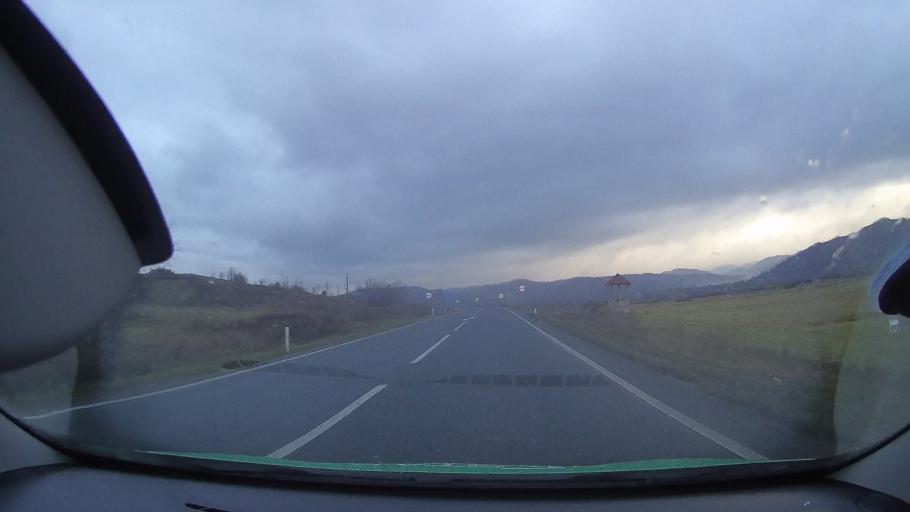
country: RO
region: Hunedoara
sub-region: Comuna Ribita
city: Ribita
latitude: 46.1598
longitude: 22.7619
